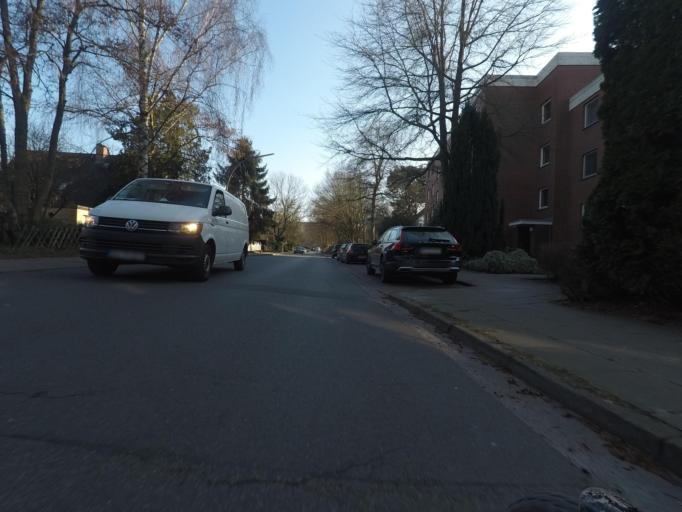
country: DE
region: Hamburg
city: Farmsen-Berne
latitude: 53.6021
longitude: 10.0955
